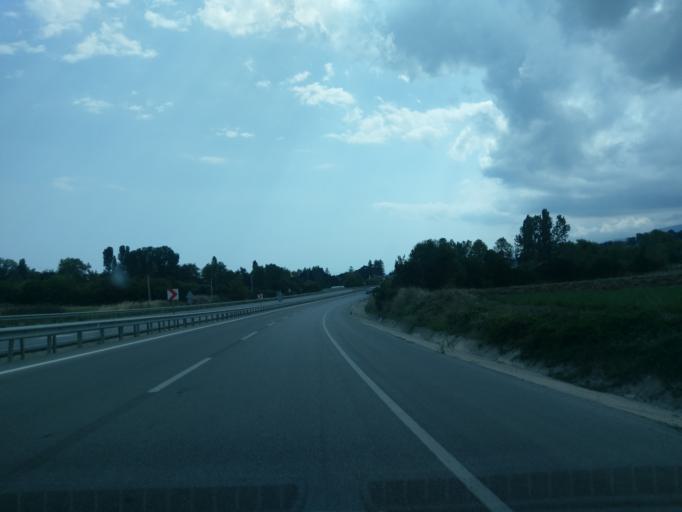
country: TR
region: Sinop
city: Gerze
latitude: 41.8399
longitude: 35.1510
